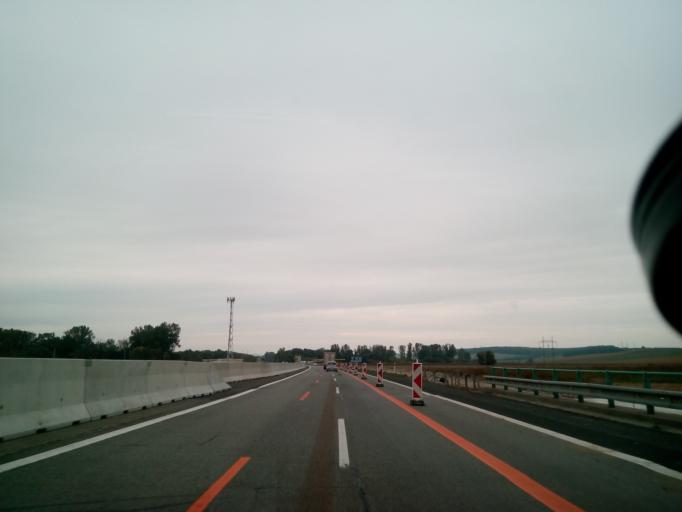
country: SK
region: Kosicky
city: Kosice
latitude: 48.8315
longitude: 21.3069
